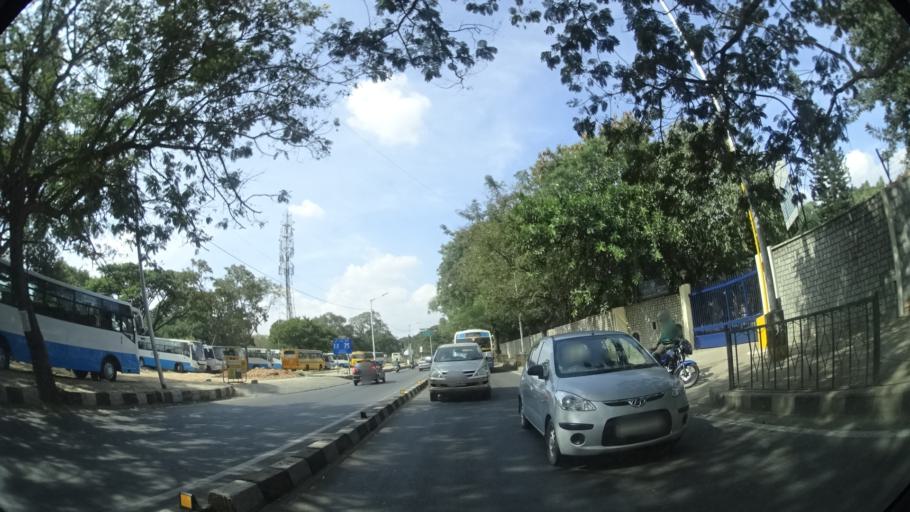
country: IN
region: Karnataka
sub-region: Bangalore Urban
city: Bangalore
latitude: 13.0095
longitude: 77.5909
